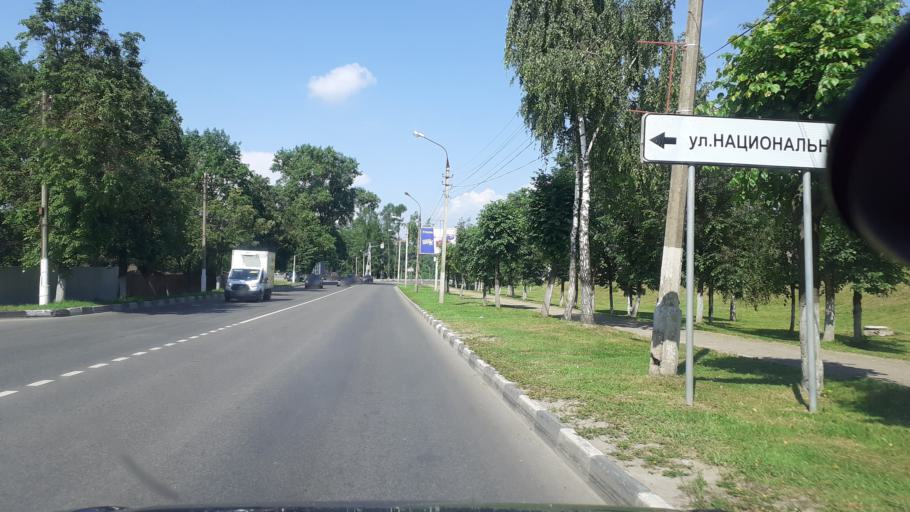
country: RU
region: Moskovskaya
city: Naro-Fominsk
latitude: 55.3828
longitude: 36.7408
